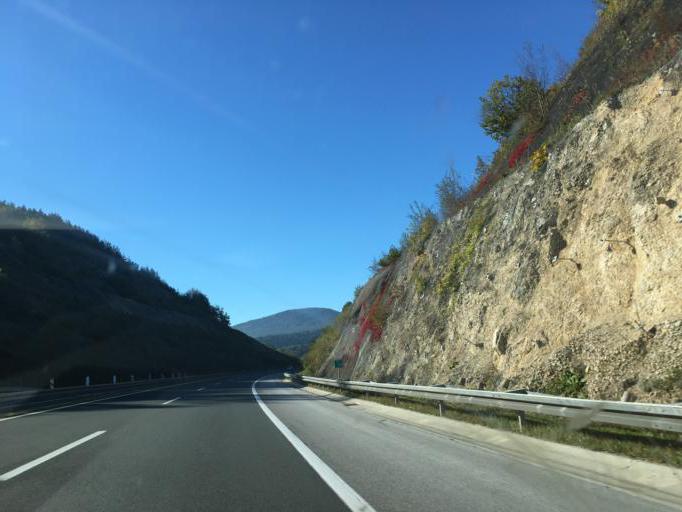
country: HR
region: Karlovacka
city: Ostarije
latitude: 45.1472
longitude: 15.2738
